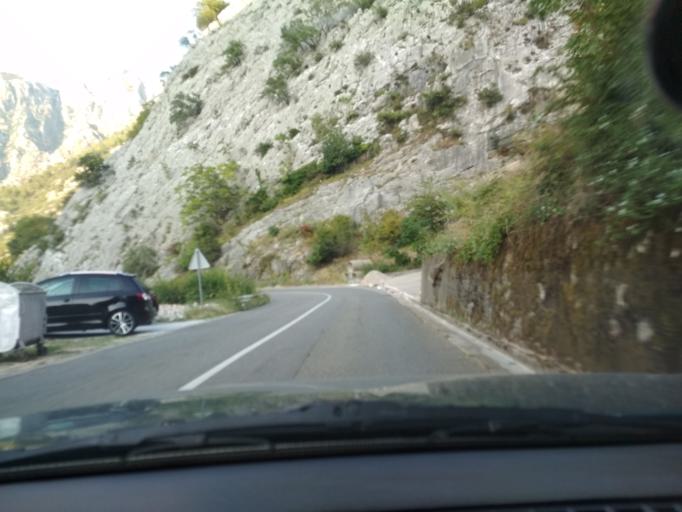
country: ME
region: Kotor
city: Kotor
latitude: 42.4081
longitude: 18.7686
